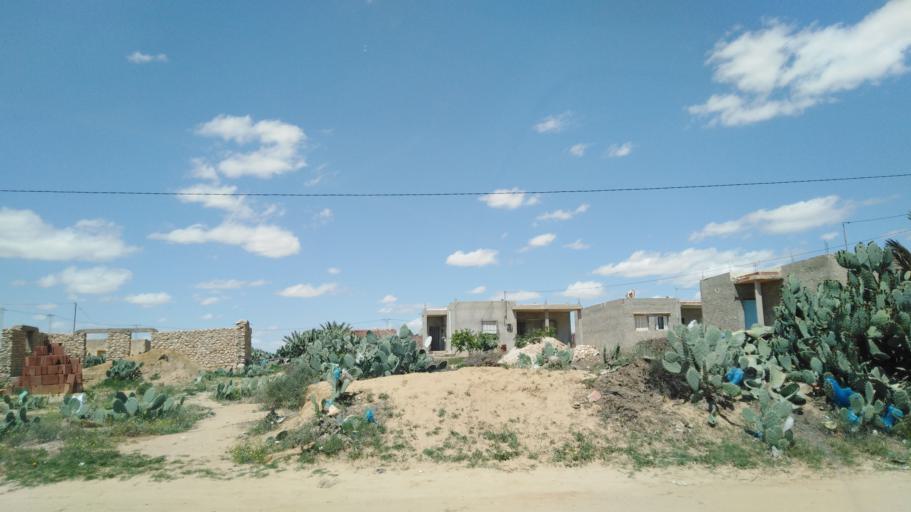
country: TN
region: Safaqis
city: Sfax
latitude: 34.7484
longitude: 10.5386
